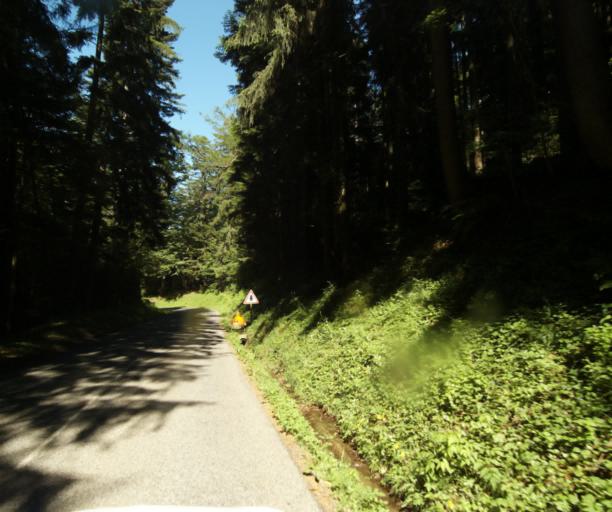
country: FR
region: Rhone-Alpes
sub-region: Departement de la Haute-Savoie
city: Bons-en-Chablais
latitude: 46.2545
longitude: 6.3853
